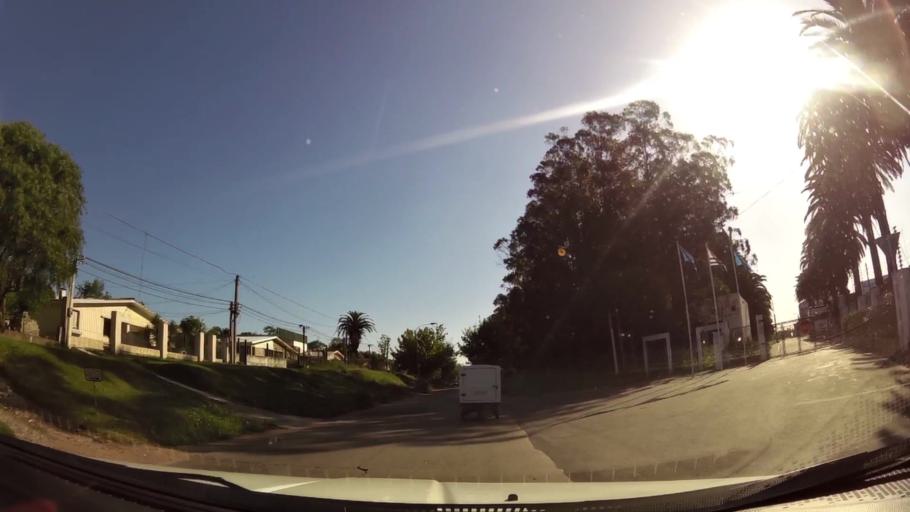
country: UY
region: Canelones
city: La Paz
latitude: -34.8227
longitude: -56.1786
